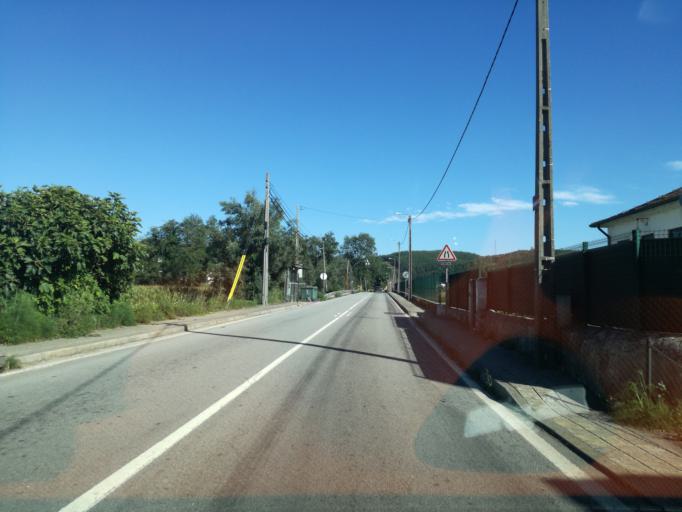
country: PT
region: Porto
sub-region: Valongo
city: Alfena
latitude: 41.2595
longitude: -8.4833
